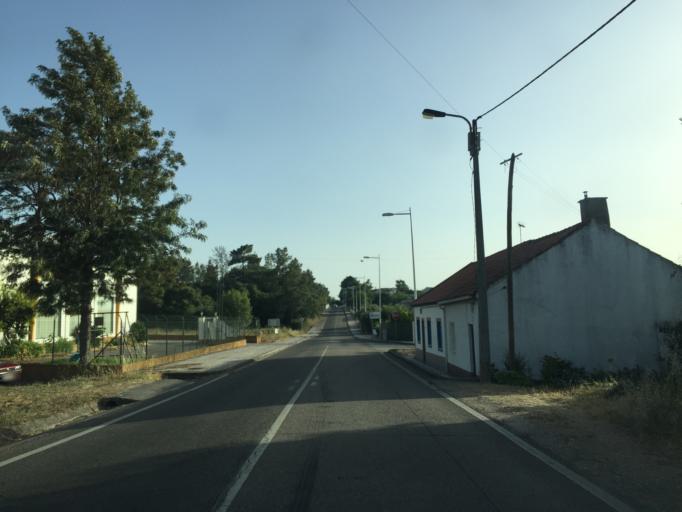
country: PT
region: Santarem
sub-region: Entroncamento
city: Entroncamento
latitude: 39.4849
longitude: -8.4480
